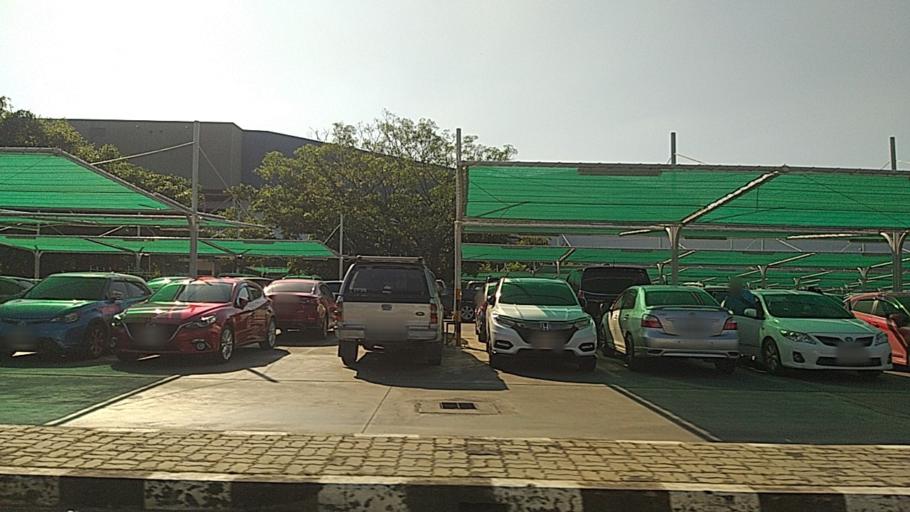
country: TH
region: Phra Nakhon Si Ayutthaya
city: Ban Bang Kadi Pathum Thani
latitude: 13.9897
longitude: 100.6203
